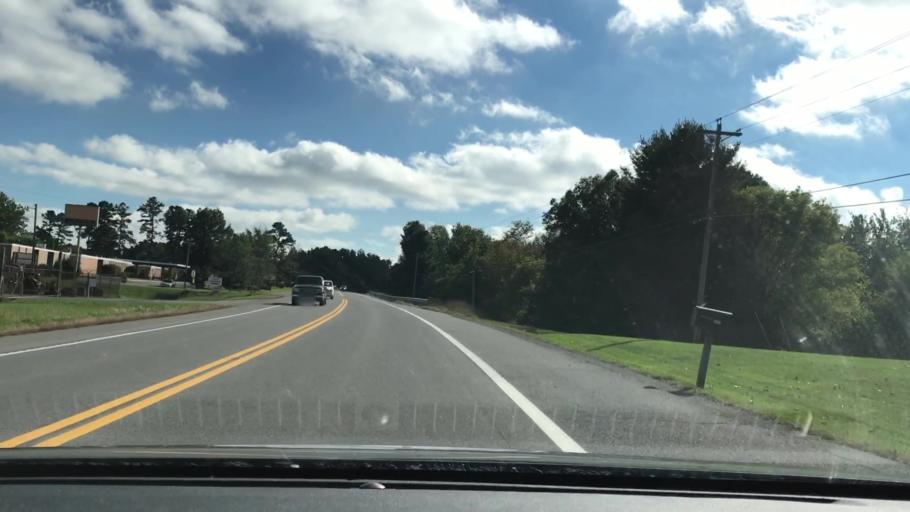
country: US
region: Tennessee
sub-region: Fentress County
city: Grimsley
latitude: 36.2397
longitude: -85.0060
